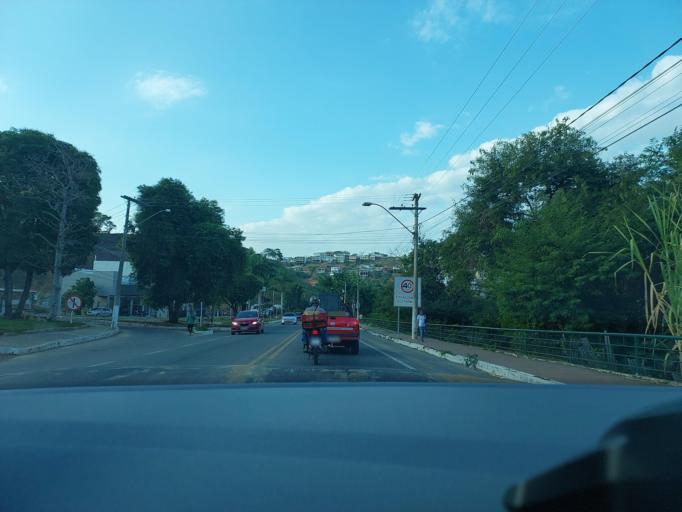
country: BR
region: Minas Gerais
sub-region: Muriae
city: Muriae
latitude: -21.1281
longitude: -42.3579
